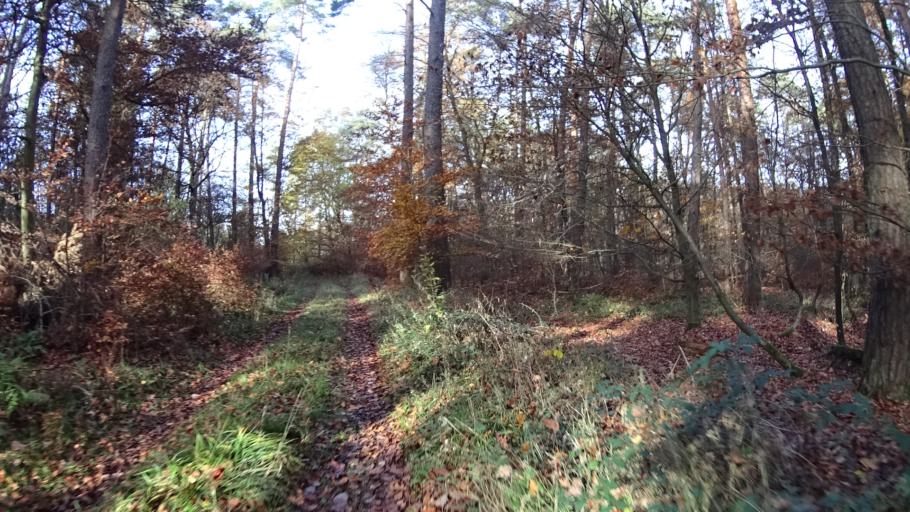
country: DE
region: Rheinland-Pfalz
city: Unterjeckenbach
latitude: 49.6777
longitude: 7.4823
